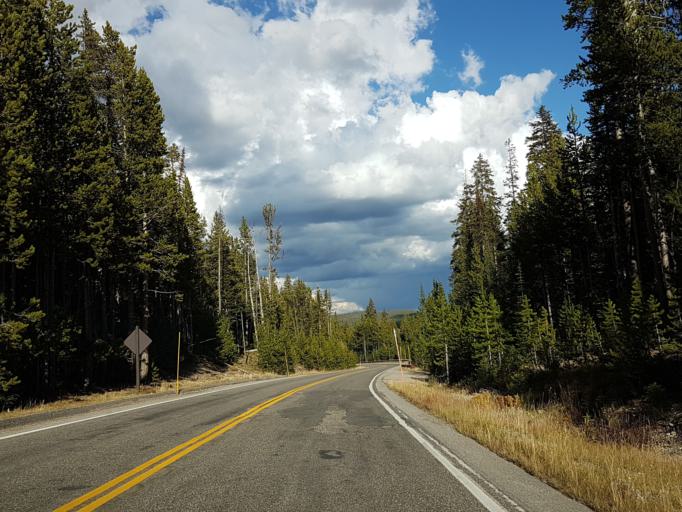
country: US
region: Montana
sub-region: Gallatin County
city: West Yellowstone
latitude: 44.4424
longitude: -110.7170
